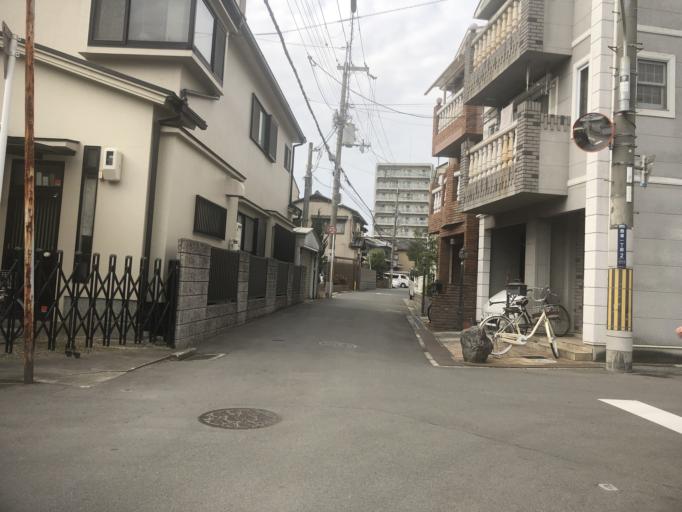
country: JP
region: Osaka
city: Moriguchi
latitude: 34.6778
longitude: 135.5762
